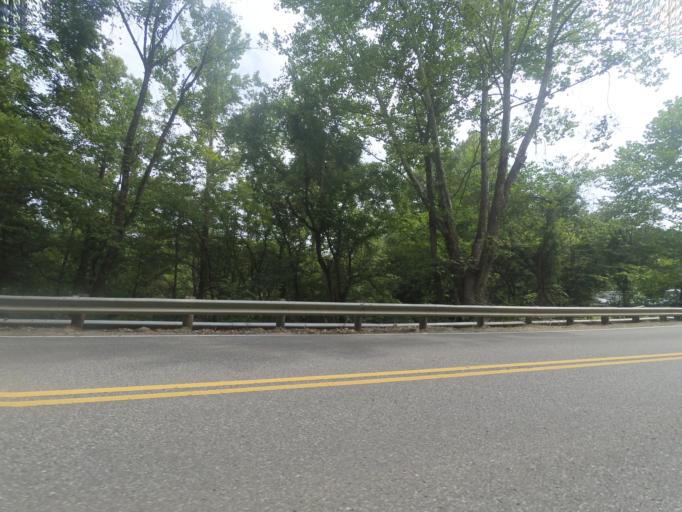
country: US
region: West Virginia
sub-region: Cabell County
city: Huntington
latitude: 38.4309
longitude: -82.4621
